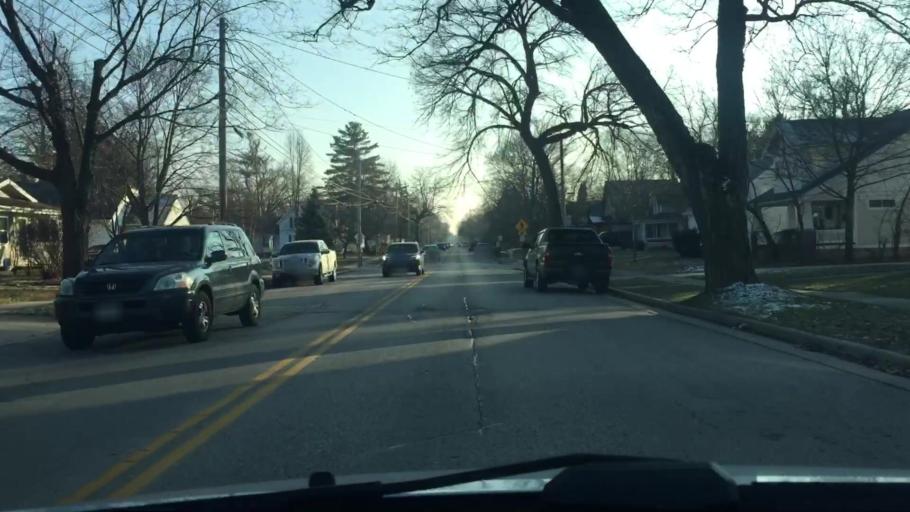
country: US
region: Wisconsin
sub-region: Waukesha County
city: Oconomowoc
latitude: 43.1058
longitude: -88.4959
